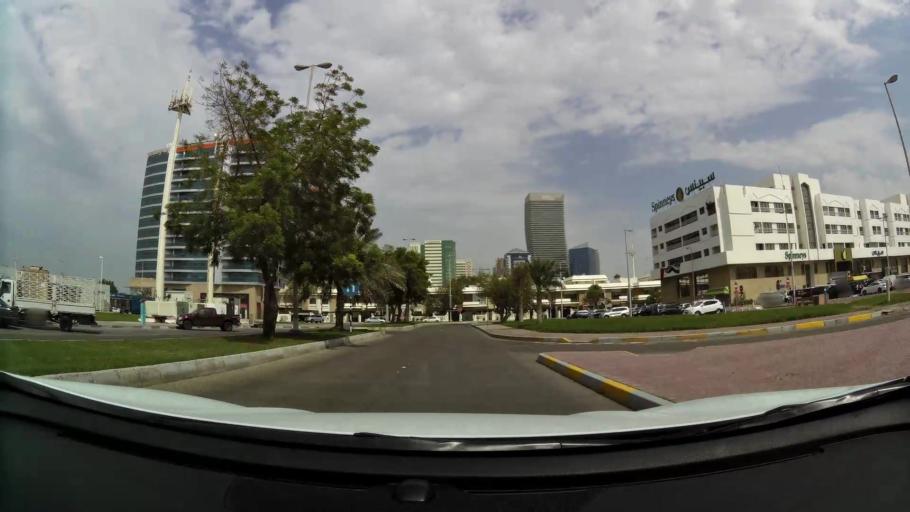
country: AE
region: Abu Dhabi
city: Abu Dhabi
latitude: 24.4659
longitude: 54.3335
